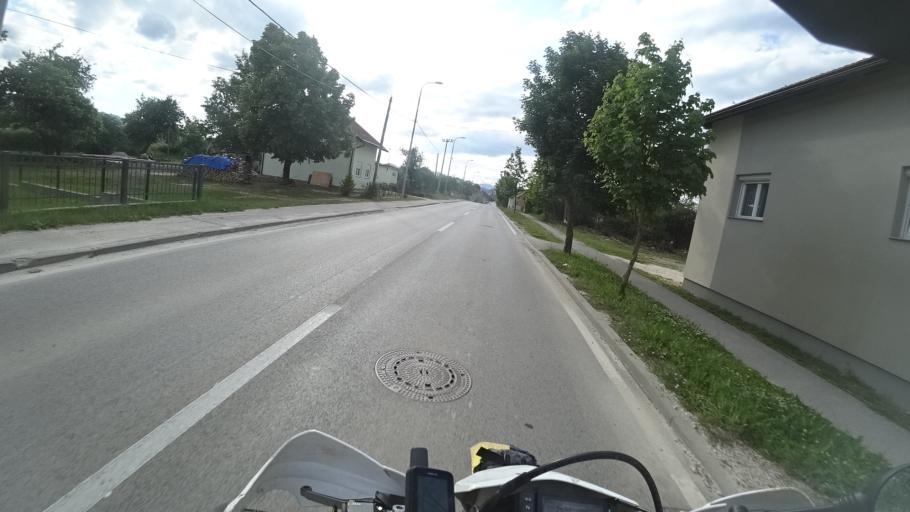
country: HR
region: Licko-Senjska
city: Gospic
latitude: 44.5363
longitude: 15.3910
